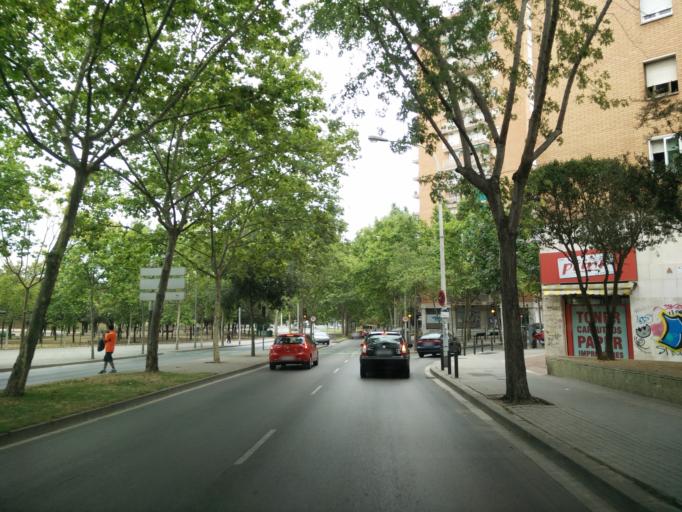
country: ES
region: Catalonia
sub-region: Provincia de Barcelona
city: Llefia
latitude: 41.4531
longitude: 2.2295
